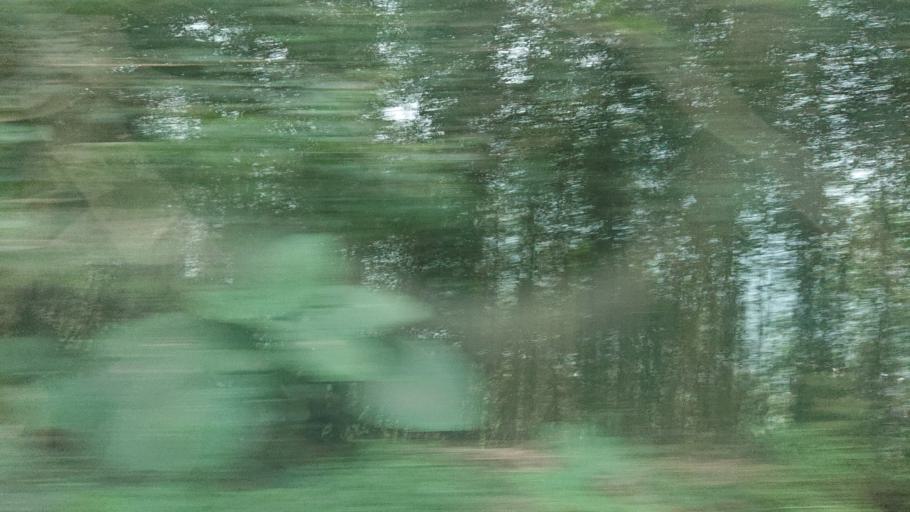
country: TW
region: Taiwan
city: Lugu
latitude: 23.6030
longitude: 120.7071
